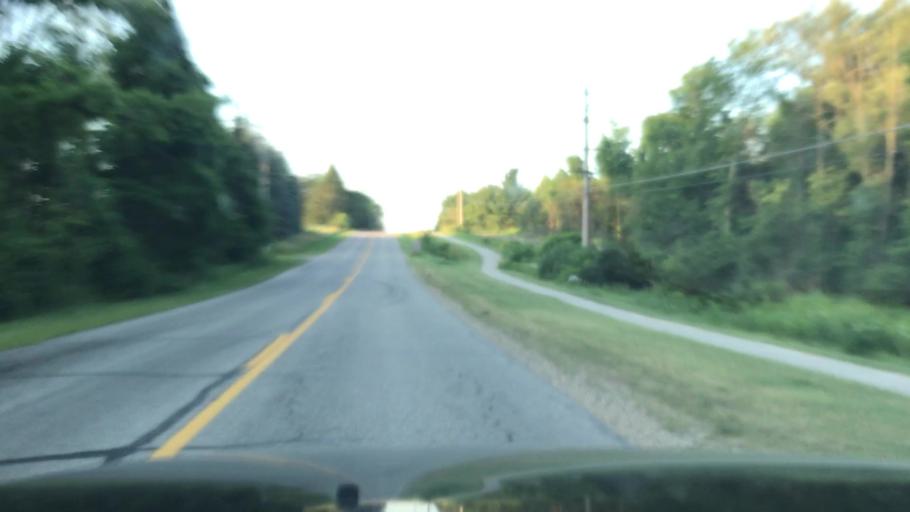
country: US
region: Michigan
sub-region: Ottawa County
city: Zeeland
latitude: 42.7806
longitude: -86.0578
